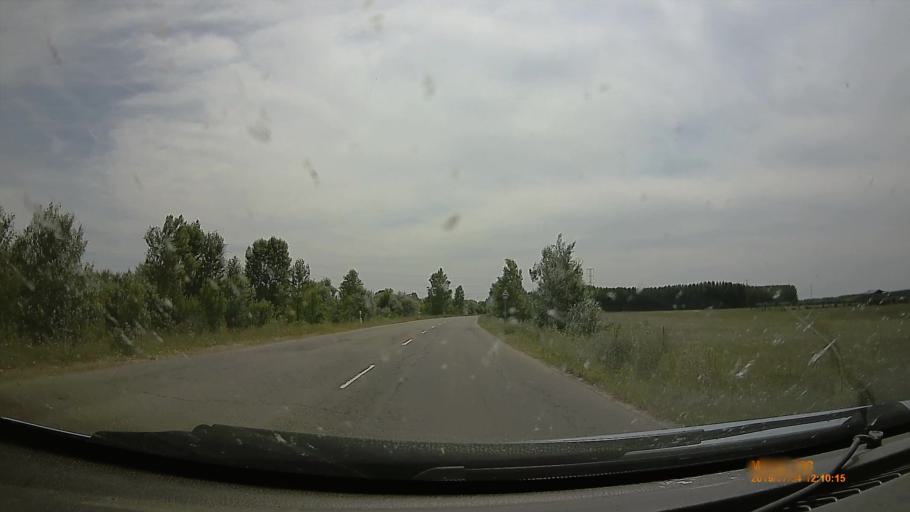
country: HU
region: Pest
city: Gyal
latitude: 47.3851
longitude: 19.2495
